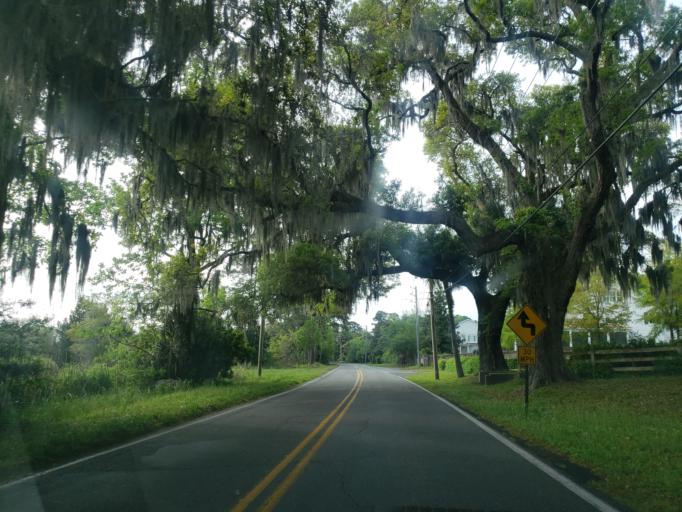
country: US
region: Georgia
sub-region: Chatham County
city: Isle of Hope
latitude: 32.0067
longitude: -81.0653
